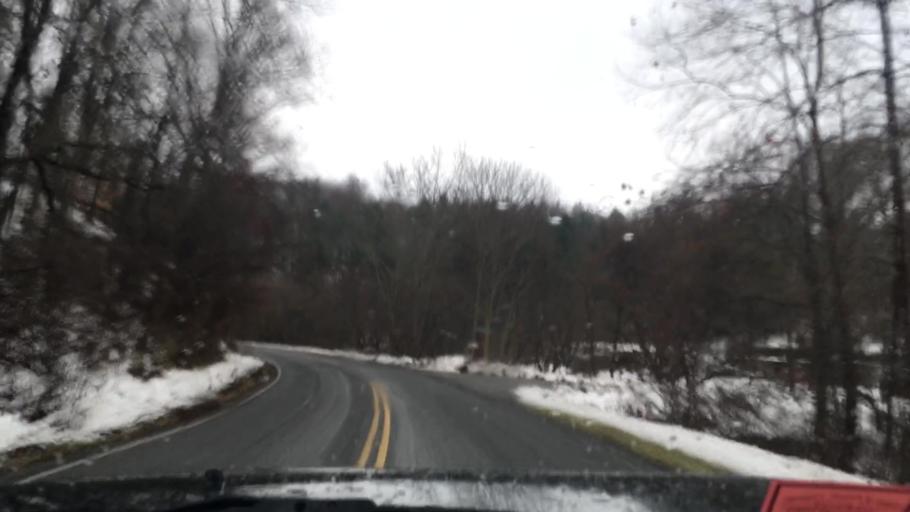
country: US
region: Virginia
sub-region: Pulaski County
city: Pulaski
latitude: 37.0142
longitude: -80.7039
